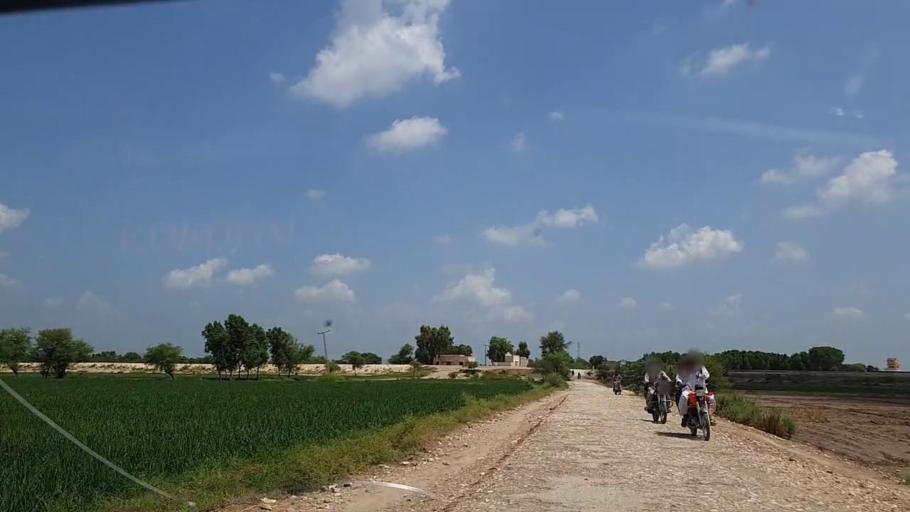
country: PK
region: Sindh
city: Tharu Shah
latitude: 26.9949
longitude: 68.0705
